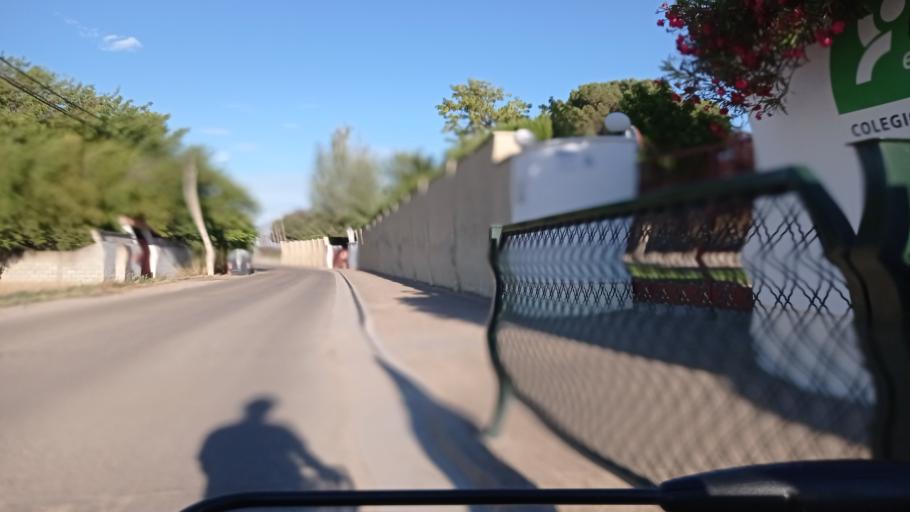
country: ES
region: Aragon
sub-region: Provincia de Zaragoza
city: Oliver-Valdefierro, Oliver, Valdefierro
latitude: 41.6749
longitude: -0.9600
